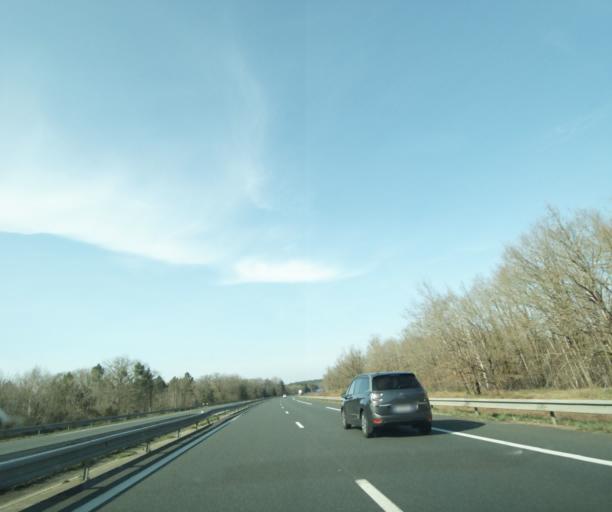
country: FR
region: Centre
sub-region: Departement du Loir-et-Cher
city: Nouan-le-Fuzelier
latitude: 47.5236
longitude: 2.0045
